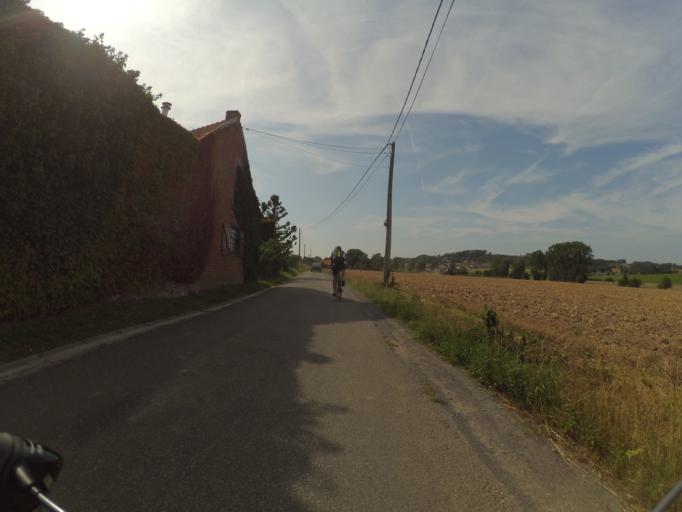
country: BE
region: Wallonia
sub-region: Province du Hainaut
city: Flobecq
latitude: 50.7256
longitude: 3.7271
